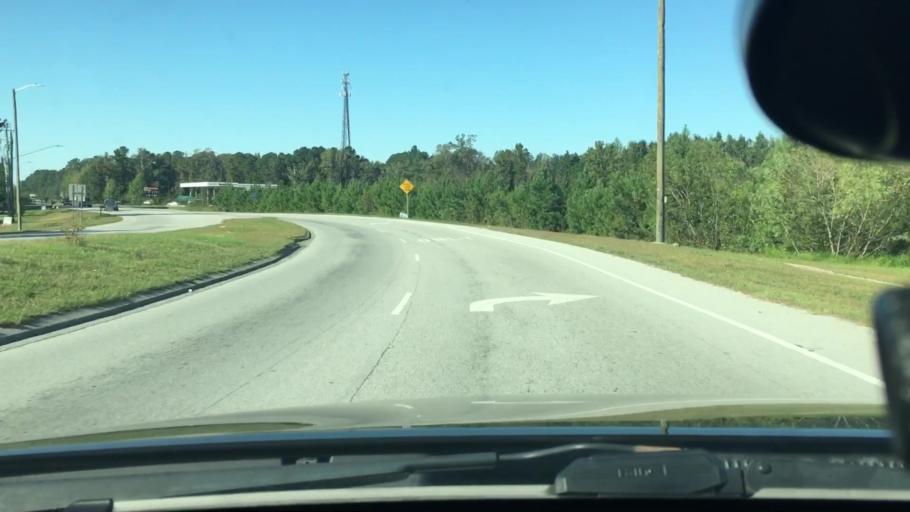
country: US
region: North Carolina
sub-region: Craven County
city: Trent Woods
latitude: 35.1453
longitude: -77.1062
